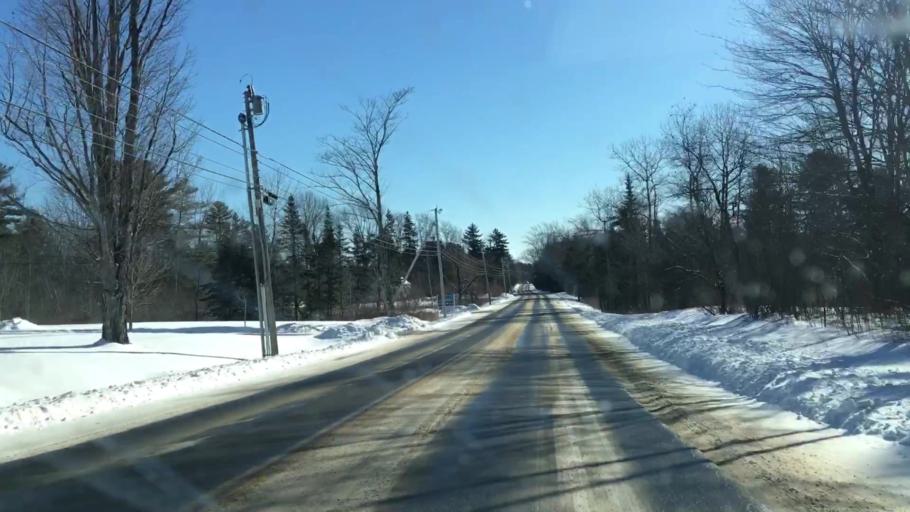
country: US
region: Maine
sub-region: Sagadahoc County
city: Topsham
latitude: 43.9091
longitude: -70.0107
